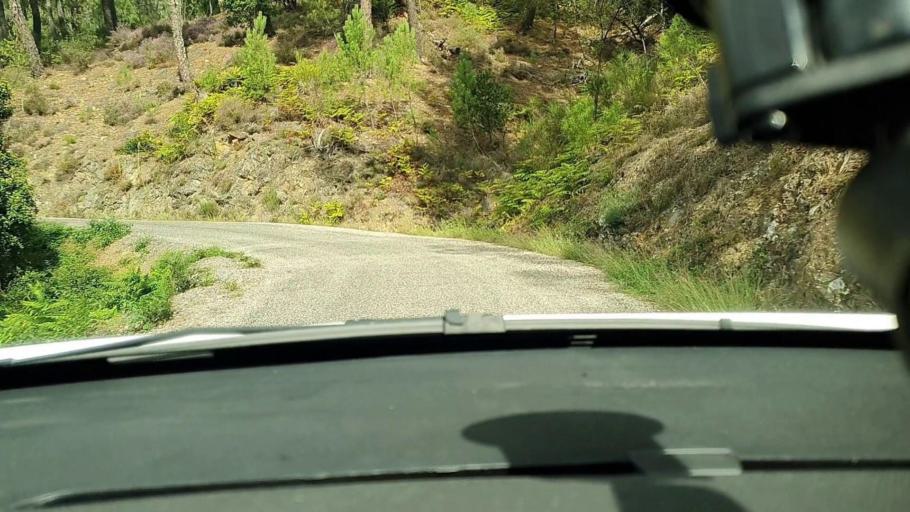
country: FR
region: Languedoc-Roussillon
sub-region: Departement du Gard
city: Branoux-les-Taillades
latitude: 44.2354
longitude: 3.9800
